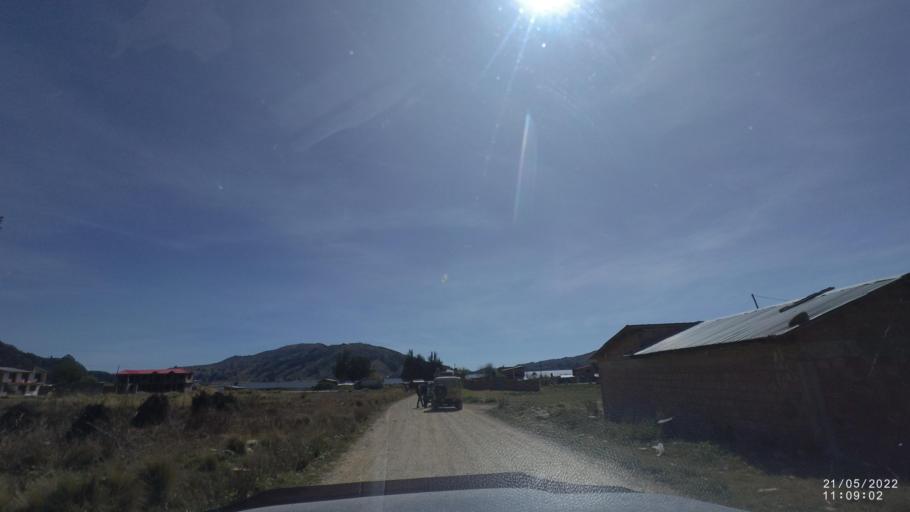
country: BO
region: Cochabamba
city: Colomi
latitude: -17.3023
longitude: -65.9111
